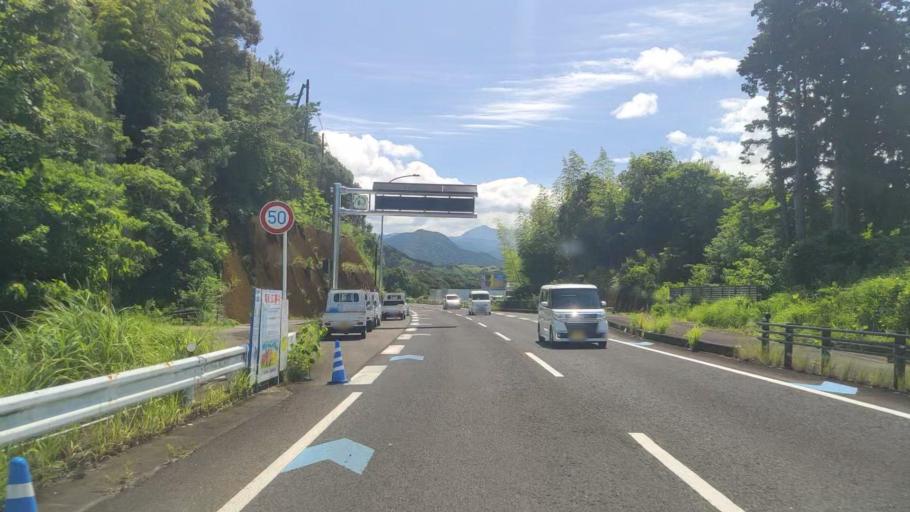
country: JP
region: Wakayama
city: Shingu
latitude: 33.7446
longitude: 136.0099
